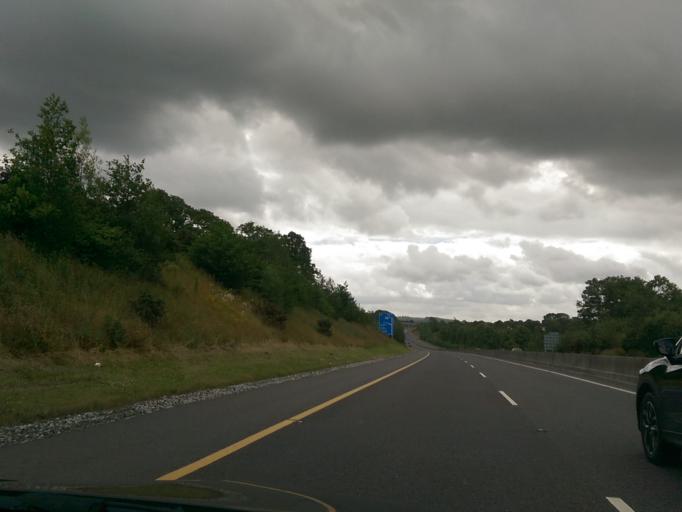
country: IE
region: Munster
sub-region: County Cork
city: Fermoy
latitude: 52.1743
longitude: -8.2710
